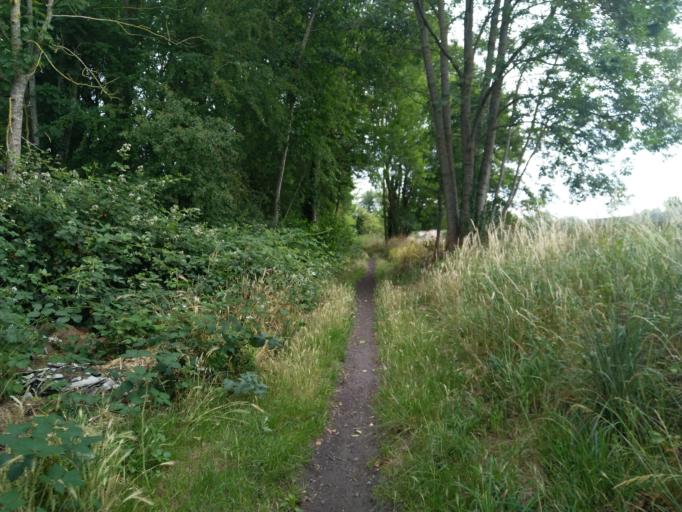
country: BE
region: Wallonia
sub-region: Province du Hainaut
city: Bernissart
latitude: 50.4751
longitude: 3.6405
